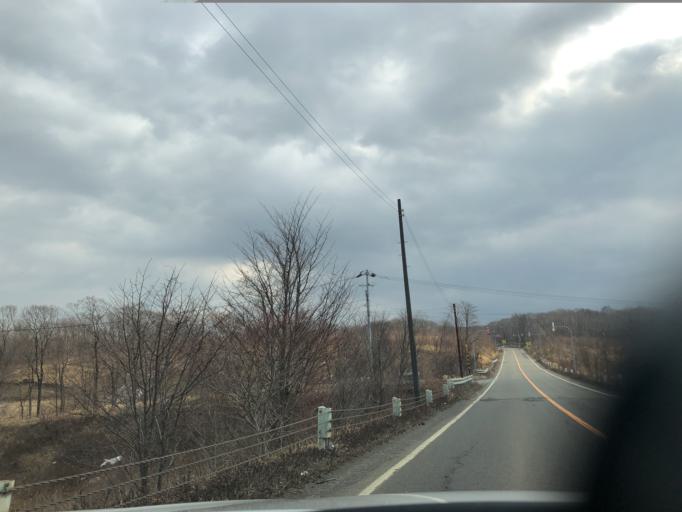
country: JP
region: Hokkaido
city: Chitose
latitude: 42.7646
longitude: 141.7222
